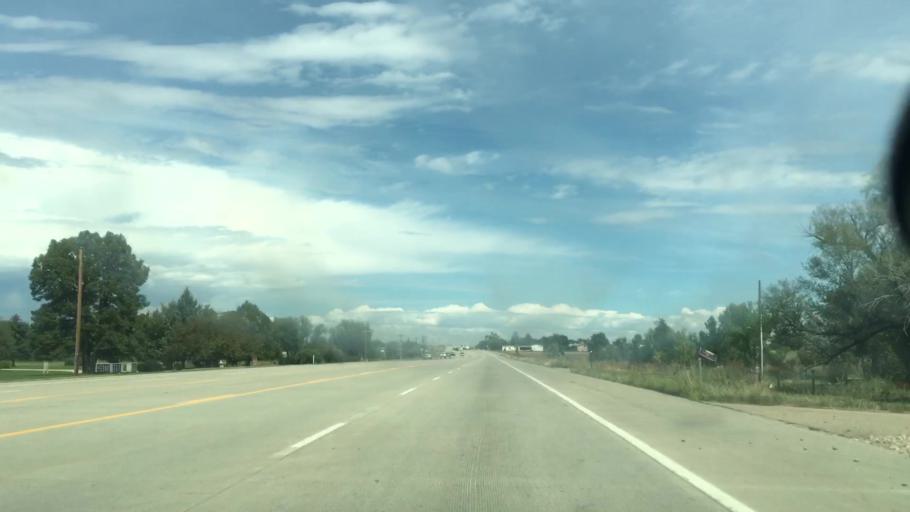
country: US
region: Colorado
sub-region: Boulder County
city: Longmont
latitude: 40.2325
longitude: -105.1022
